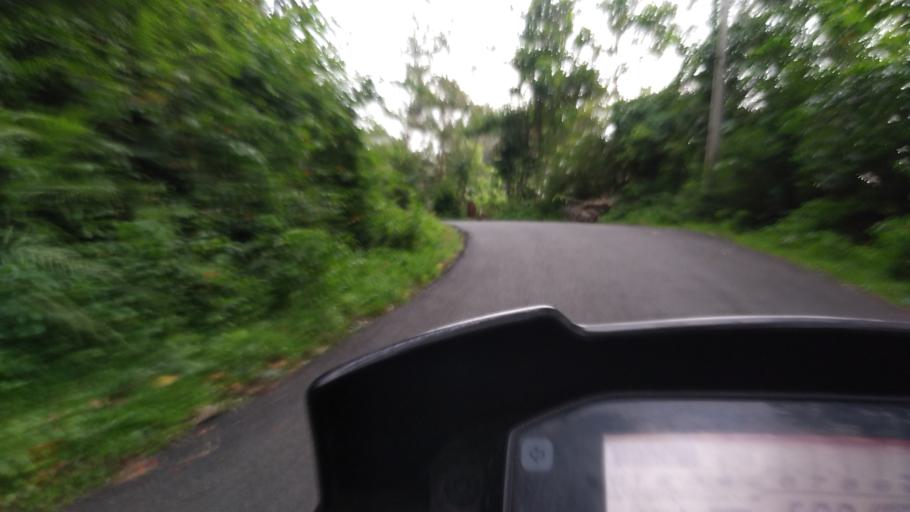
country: IN
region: Tamil Nadu
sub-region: Theni
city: Bodinayakkanur
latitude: 10.0330
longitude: 77.2293
